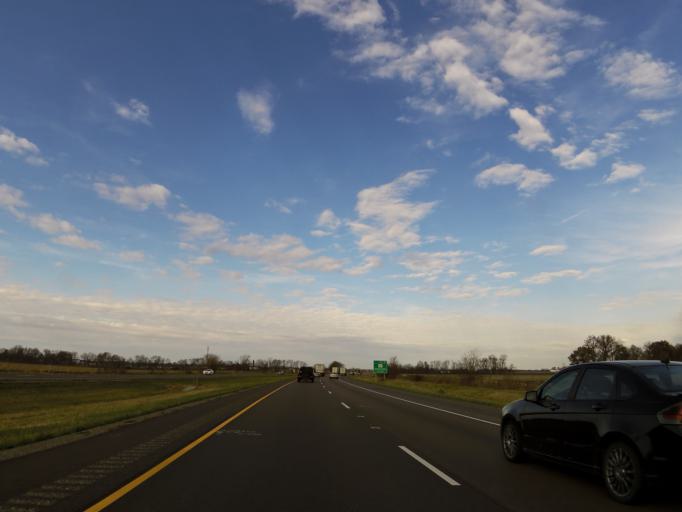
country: US
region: Illinois
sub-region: Washington County
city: Okawville
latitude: 38.4329
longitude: -89.5163
